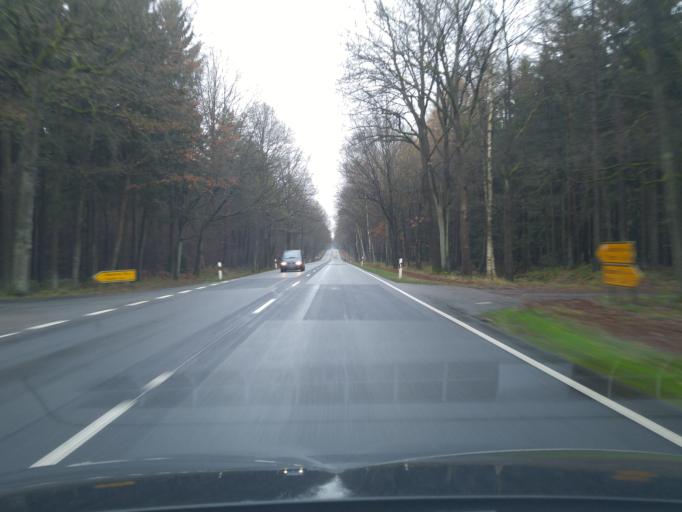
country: DE
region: Lower Saxony
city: Sprakensehl
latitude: 52.7324
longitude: 10.4853
